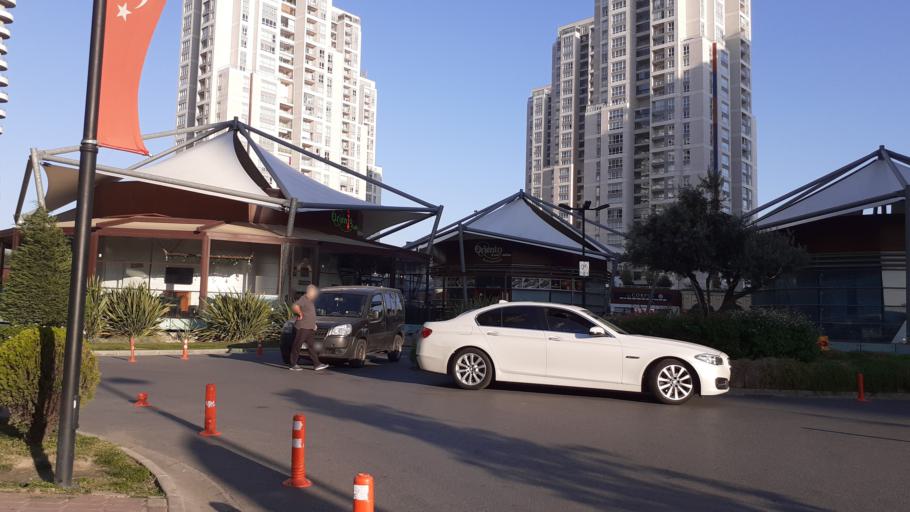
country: TR
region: Istanbul
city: Basaksehir
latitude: 41.0657
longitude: 28.7764
